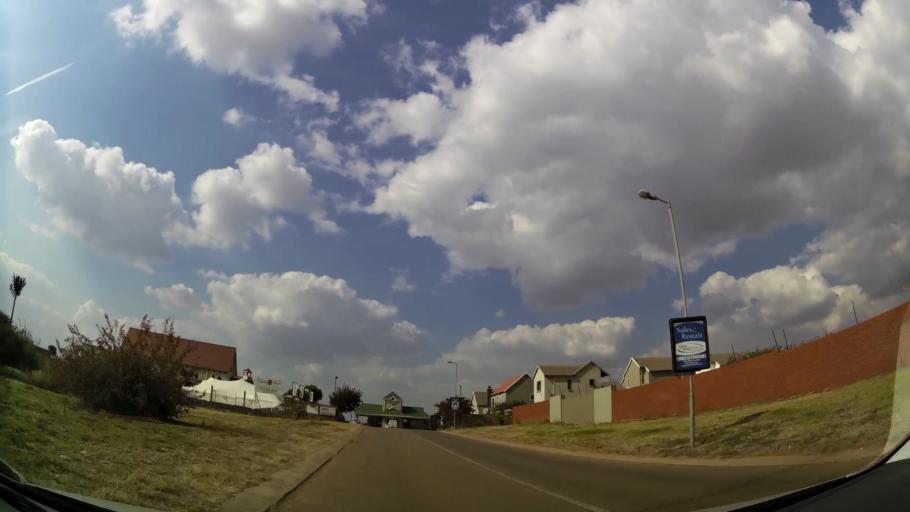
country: ZA
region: Gauteng
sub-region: City of Tshwane Metropolitan Municipality
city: Centurion
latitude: -25.9046
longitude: 28.1710
